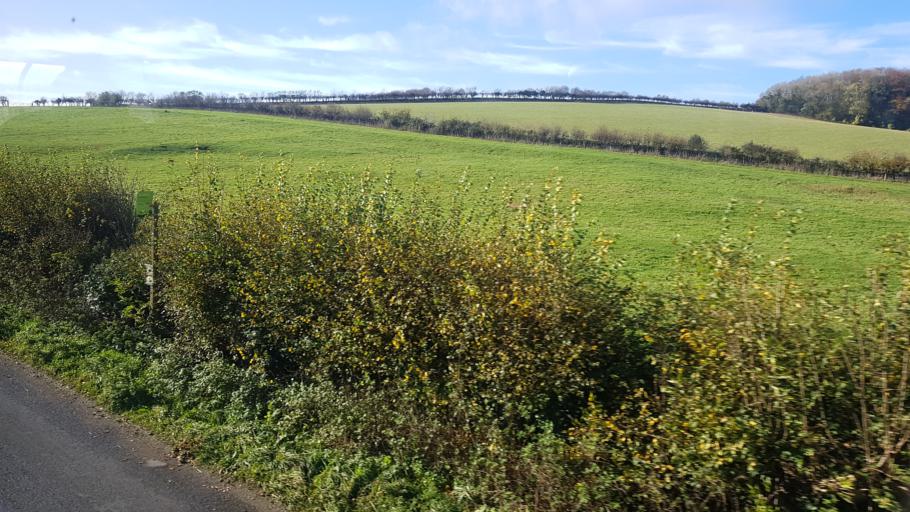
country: GB
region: England
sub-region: Isle of Wight
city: Newport
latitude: 50.6677
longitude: -1.3440
